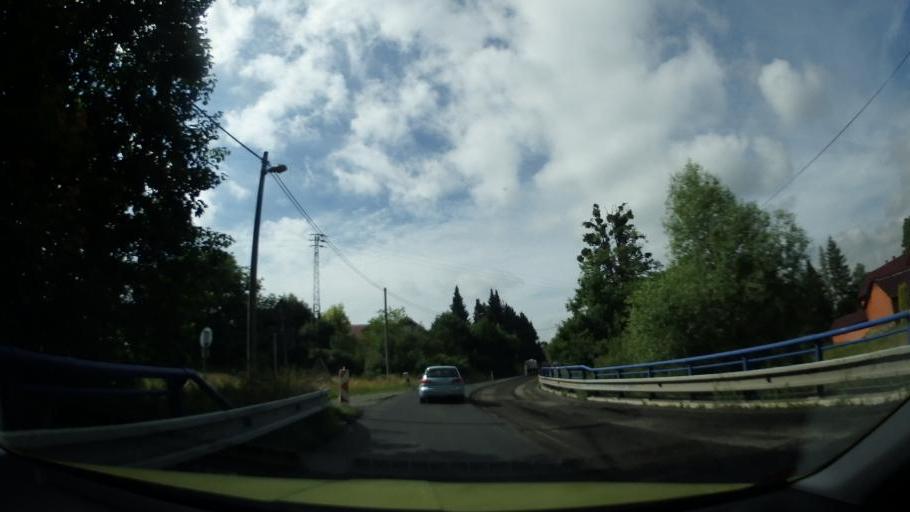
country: CZ
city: Hodslavice
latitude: 49.5573
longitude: 18.0226
